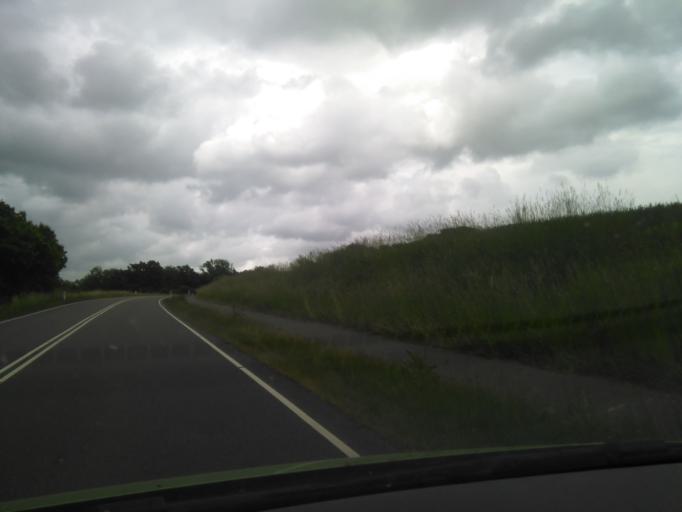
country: DK
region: Capital Region
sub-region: Bornholm Kommune
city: Akirkeby
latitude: 55.2333
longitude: 14.8761
